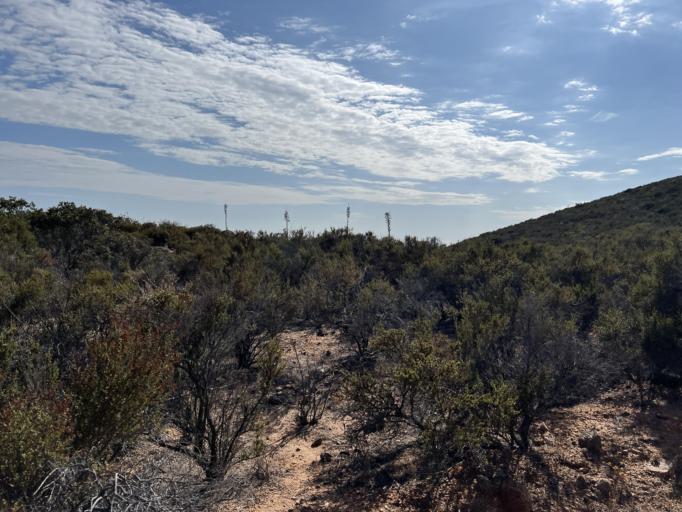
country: US
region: California
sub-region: San Diego County
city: Harbison Canyon
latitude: 32.7515
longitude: -116.8005
